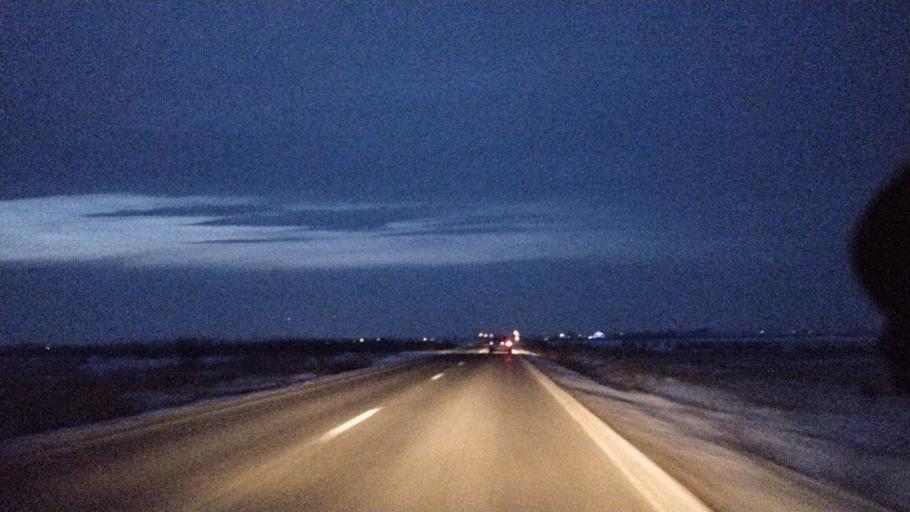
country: RO
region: Vrancea
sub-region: Comuna Milcovul
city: Milcovul
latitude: 45.6732
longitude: 27.2561
